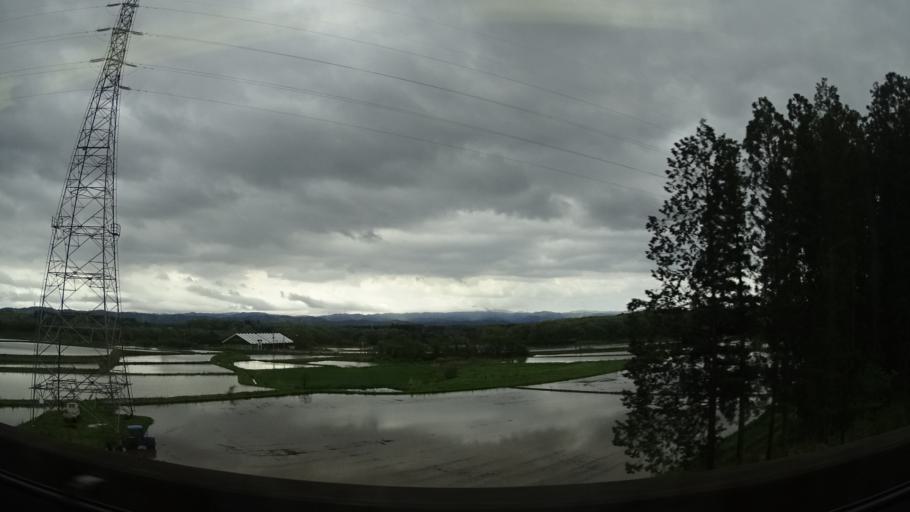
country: JP
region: Tochigi
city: Kuroiso
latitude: 37.0122
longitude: 140.0940
